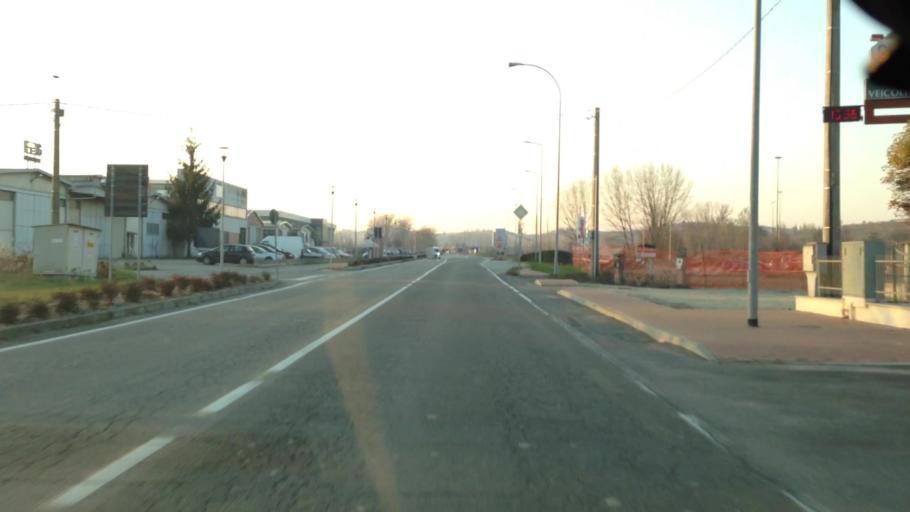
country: IT
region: Piedmont
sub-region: Provincia di Asti
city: Montegrosso
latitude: 44.8202
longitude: 8.2319
